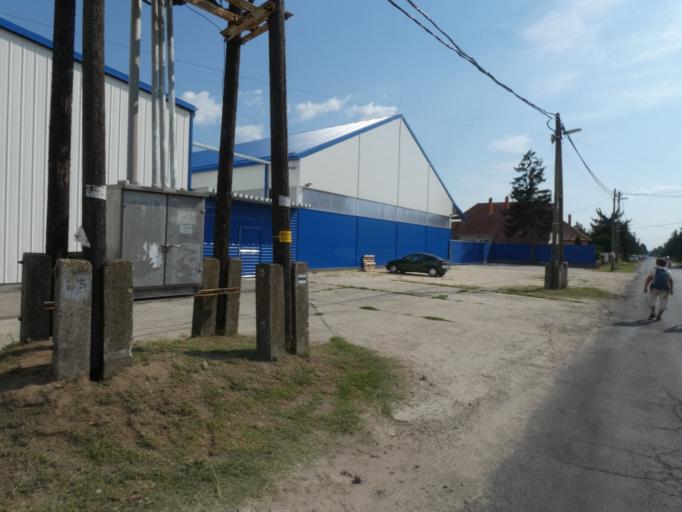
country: HU
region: Pest
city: Taborfalva
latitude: 47.1119
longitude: 19.4921
